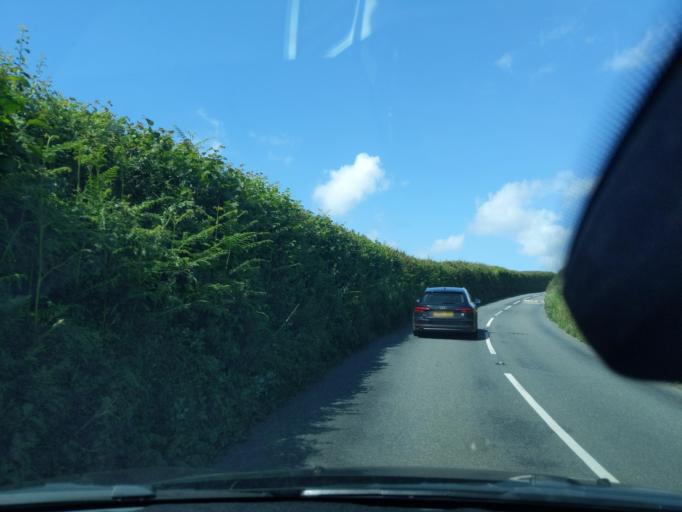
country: GB
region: England
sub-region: Devon
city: Fremington
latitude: 51.0507
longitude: -4.0904
